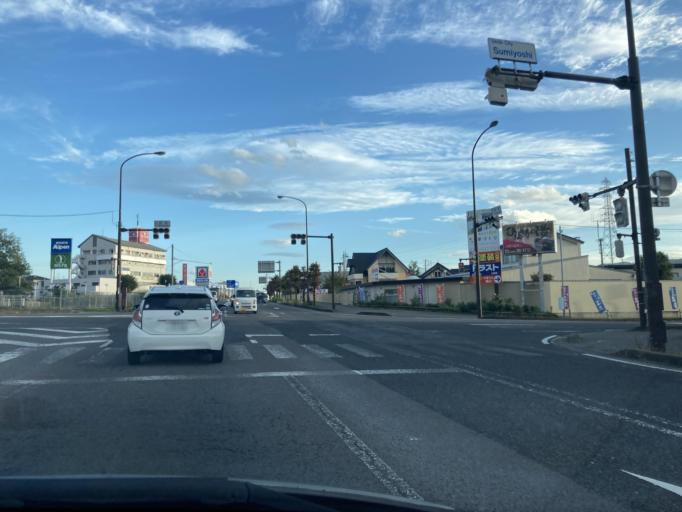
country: JP
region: Nagano
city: Ueda
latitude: 36.4042
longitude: 138.2726
